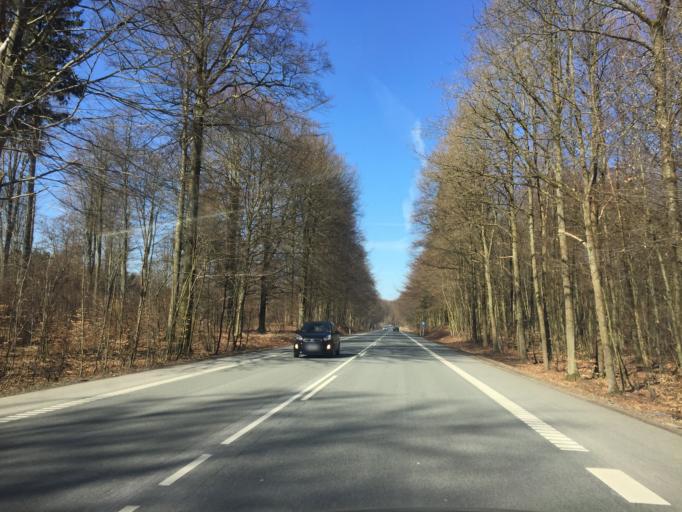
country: DK
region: Capital Region
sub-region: Fredensborg Kommune
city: Humlebaek
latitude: 56.0016
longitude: 12.4815
